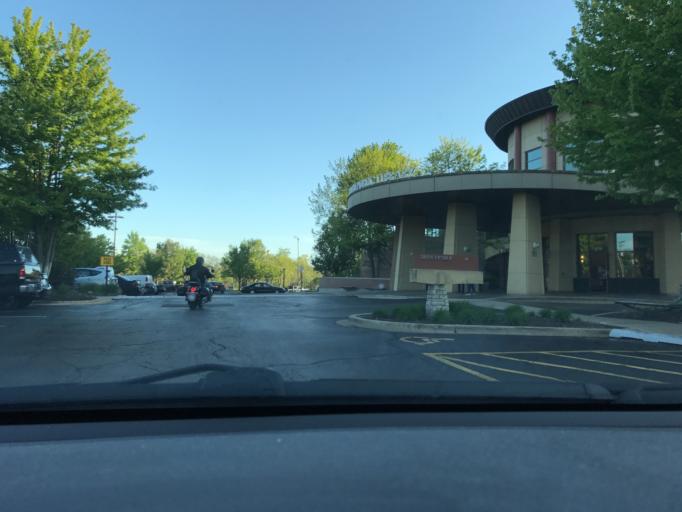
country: US
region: Illinois
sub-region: Kane County
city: Elgin
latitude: 42.0428
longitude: -88.2868
